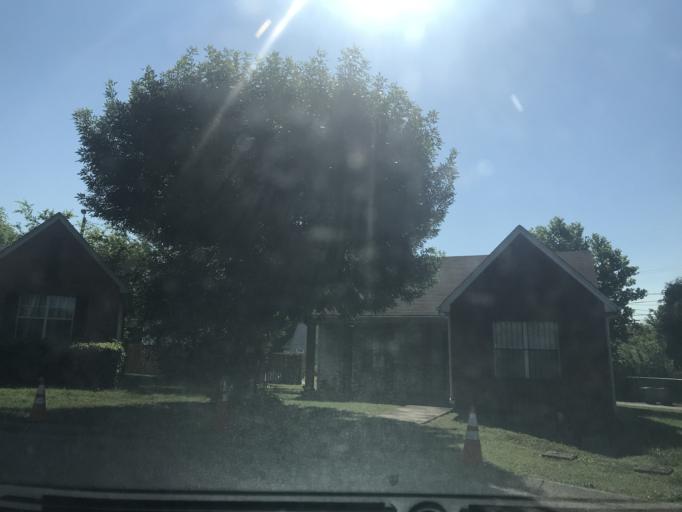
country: US
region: Tennessee
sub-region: Davidson County
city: Nashville
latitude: 36.1848
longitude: -86.8065
